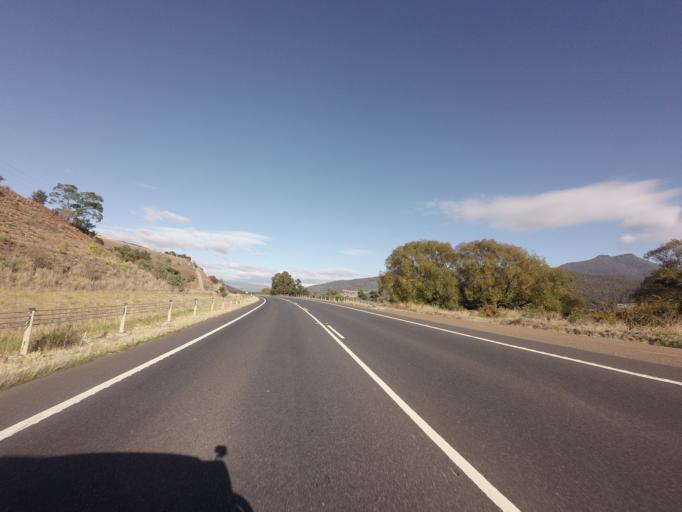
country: AU
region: Tasmania
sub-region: Glenorchy
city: Granton
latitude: -42.7455
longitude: 147.1810
